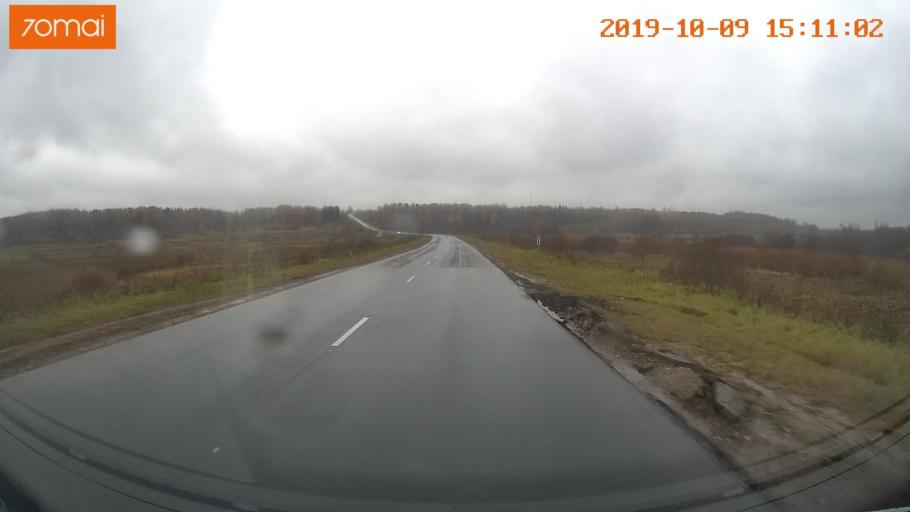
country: RU
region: Kostroma
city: Susanino
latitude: 58.1706
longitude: 41.6331
